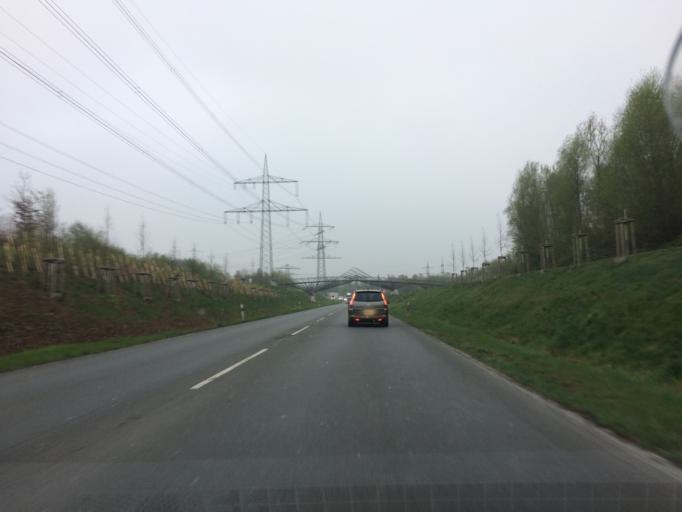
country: DE
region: North Rhine-Westphalia
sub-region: Regierungsbezirk Munster
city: Gelsenkirchen
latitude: 51.4870
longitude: 7.0982
